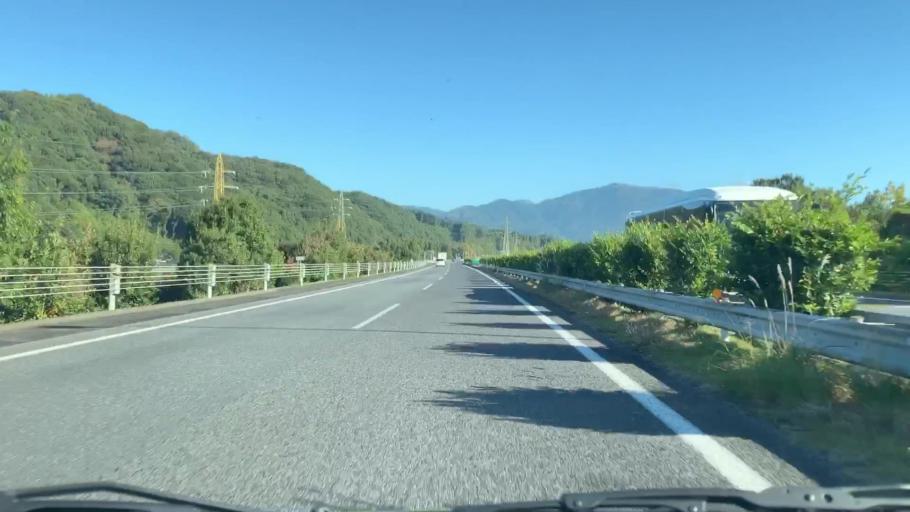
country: JP
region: Saga Prefecture
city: Takeocho-takeo
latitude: 33.2551
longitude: 130.0794
